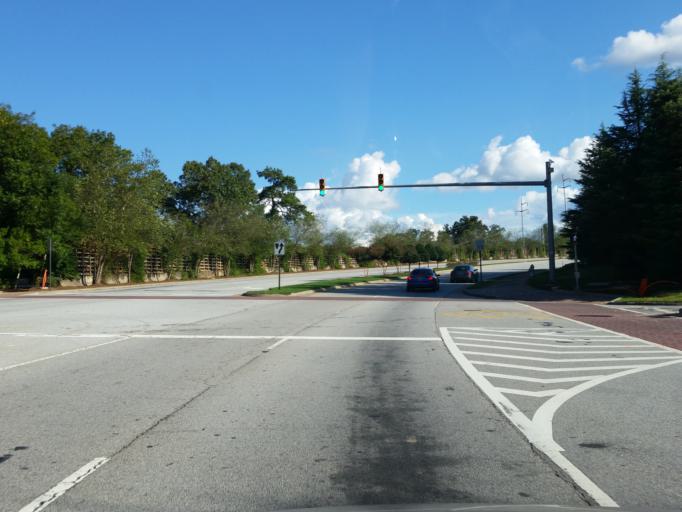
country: US
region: Georgia
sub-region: Cobb County
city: Vinings
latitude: 33.8840
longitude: -84.4524
